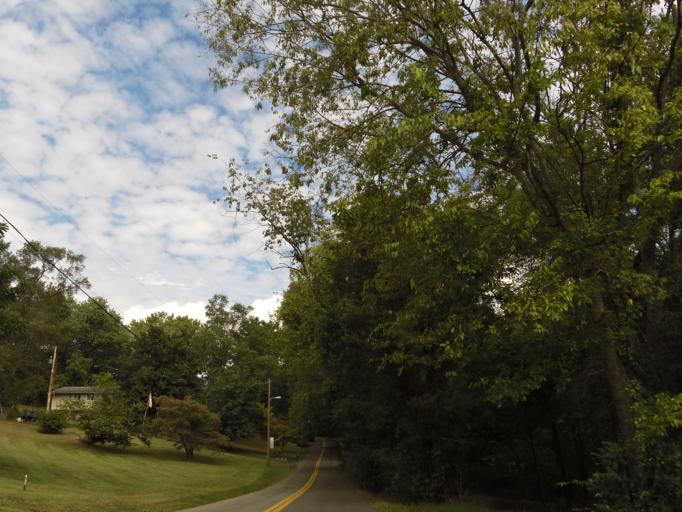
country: US
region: Tennessee
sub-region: Knox County
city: Mascot
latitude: 36.0050
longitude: -83.8282
